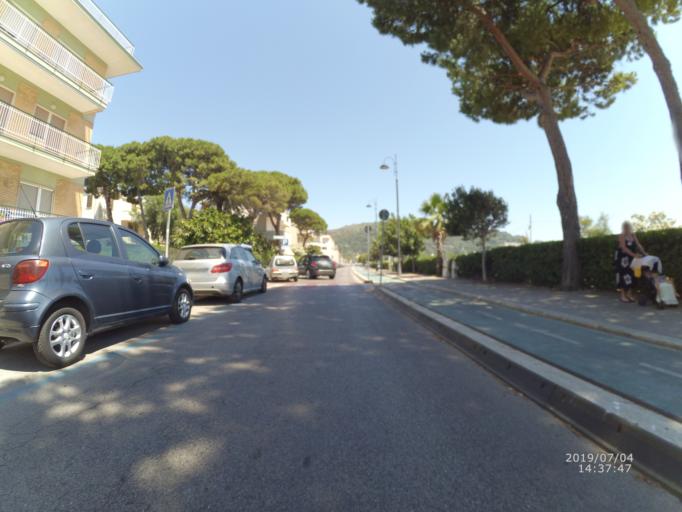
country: IT
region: Latium
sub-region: Provincia di Latina
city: Gaeta
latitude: 41.2114
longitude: 13.5635
